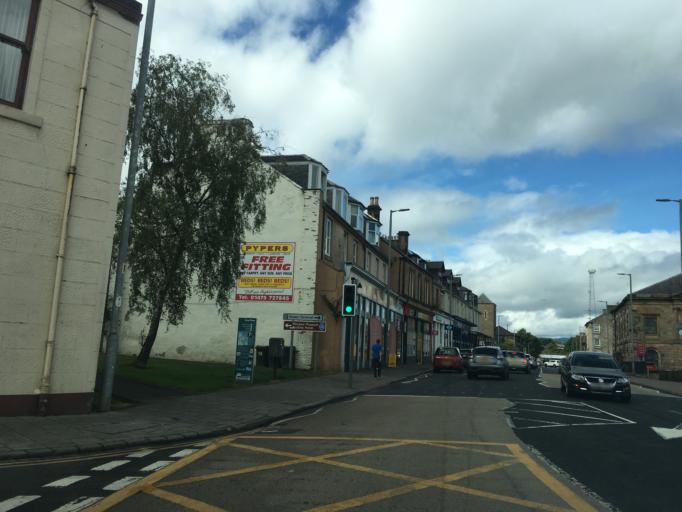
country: GB
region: Scotland
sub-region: Inverclyde
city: Greenock
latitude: 55.9524
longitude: -4.7630
